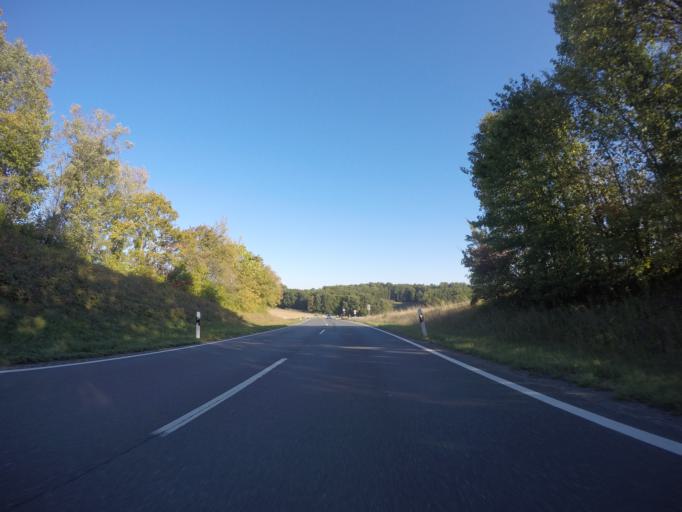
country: DE
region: Bavaria
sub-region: Regierungsbezirk Unterfranken
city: Esselbach
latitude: 49.8314
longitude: 9.5623
